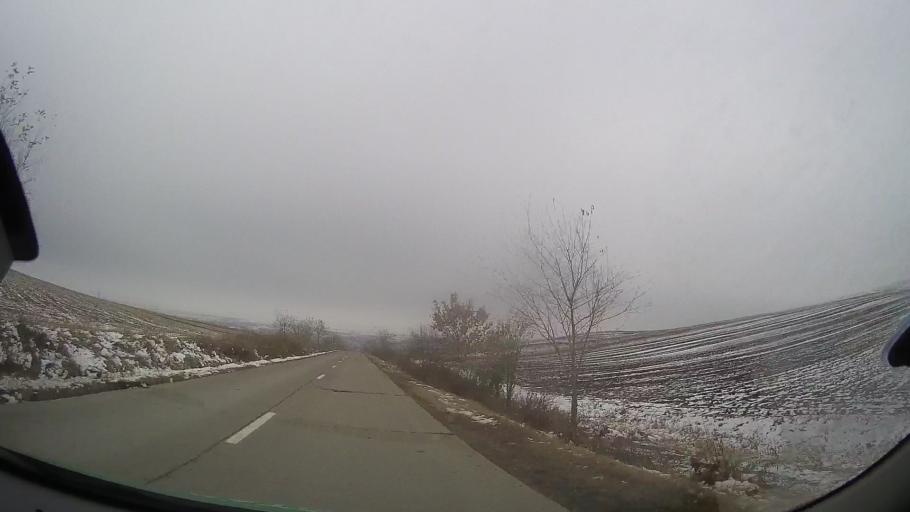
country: RO
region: Vaslui
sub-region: Comuna Ivesti
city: Ivesti
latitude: 46.1974
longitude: 27.5162
